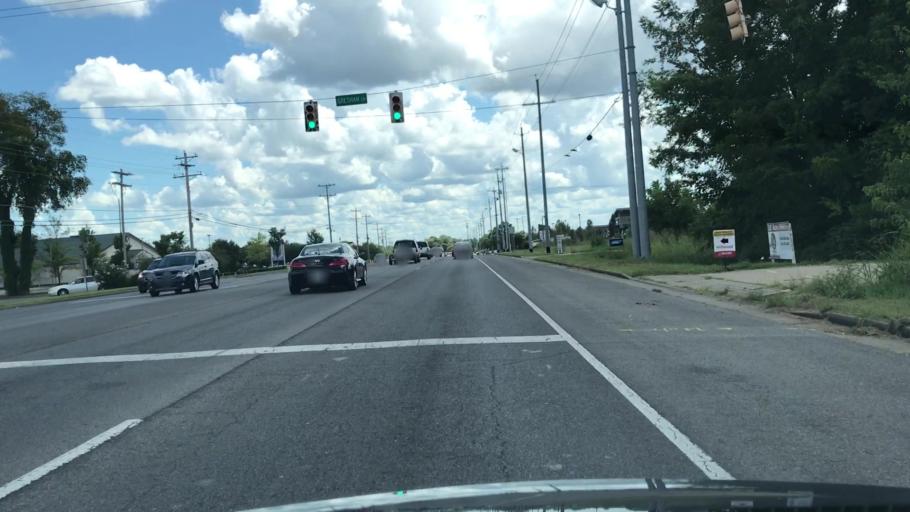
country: US
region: Tennessee
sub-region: Rutherford County
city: Murfreesboro
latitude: 35.8448
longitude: -86.4506
